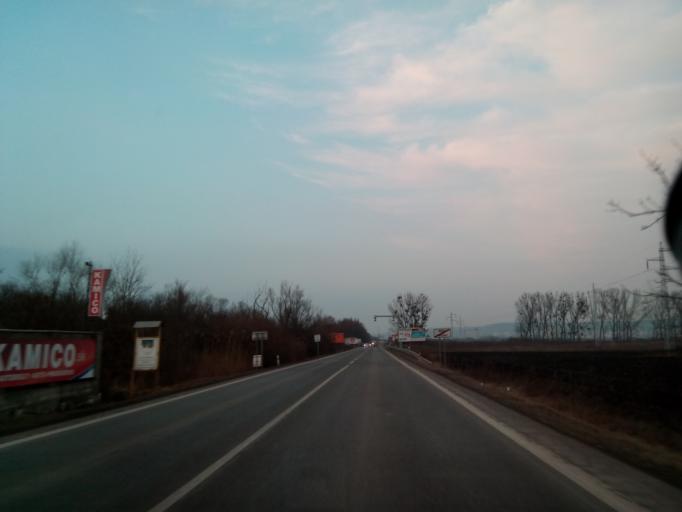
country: SK
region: Kosicky
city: Kosice
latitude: 48.6581
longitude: 21.2709
